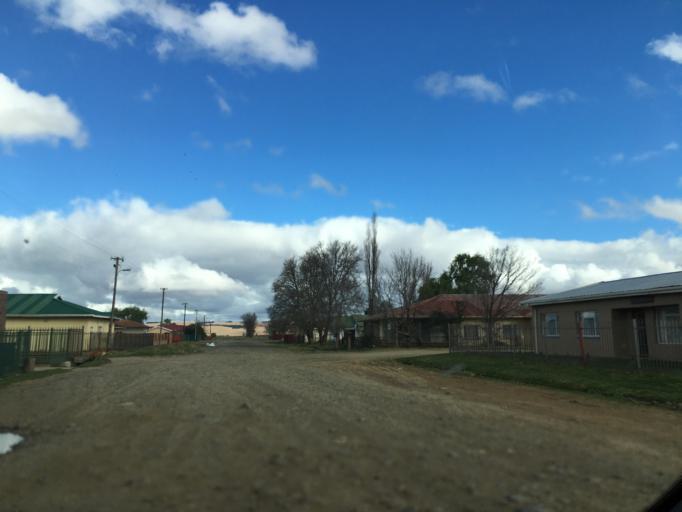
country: ZA
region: Eastern Cape
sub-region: Chris Hani District Municipality
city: Elliot
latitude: -31.3364
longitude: 27.8476
